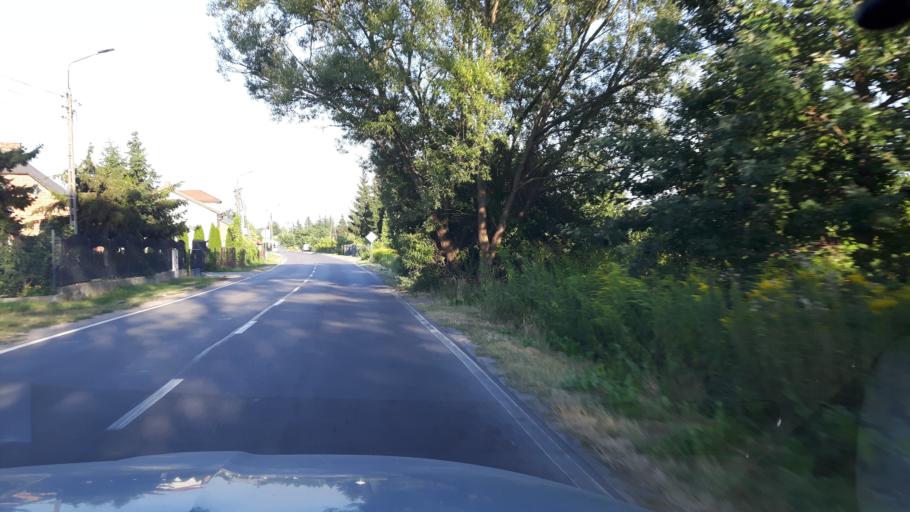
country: PL
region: Masovian Voivodeship
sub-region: Powiat wolominski
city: Kobylka
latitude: 52.3597
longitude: 21.1752
